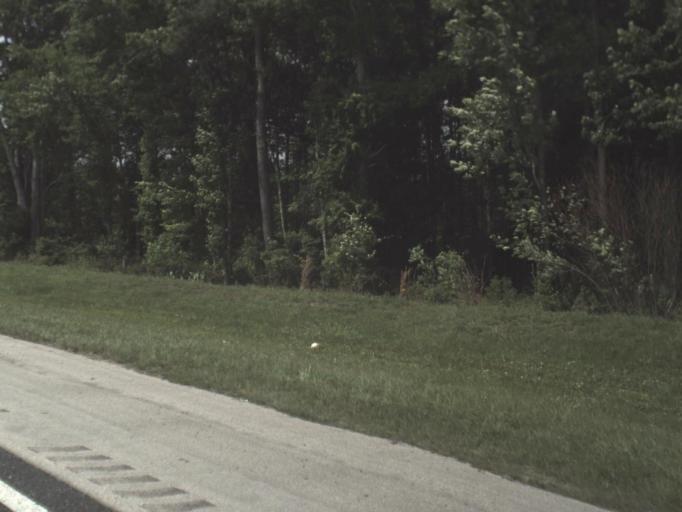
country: US
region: Florida
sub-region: Saint Johns County
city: Saint Augustine
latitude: 29.9512
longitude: -81.4397
